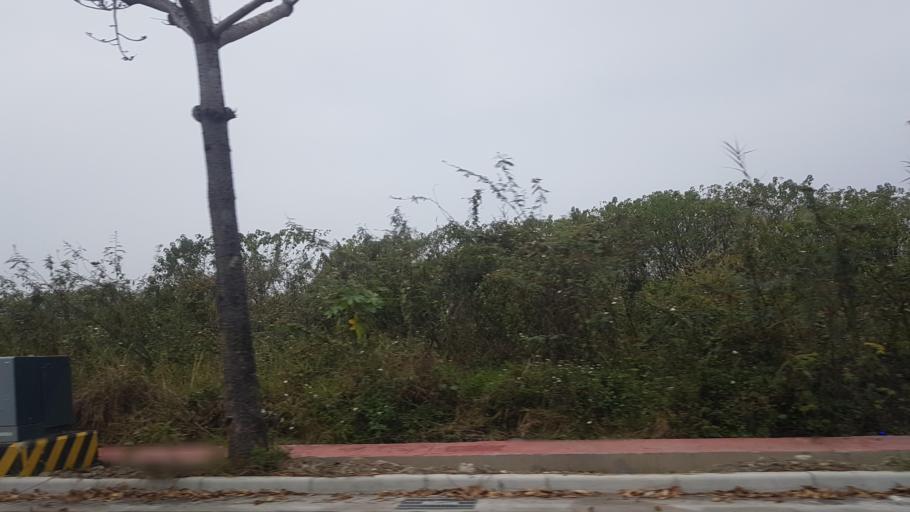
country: TW
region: Taiwan
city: Xinying
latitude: 23.3170
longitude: 120.3039
